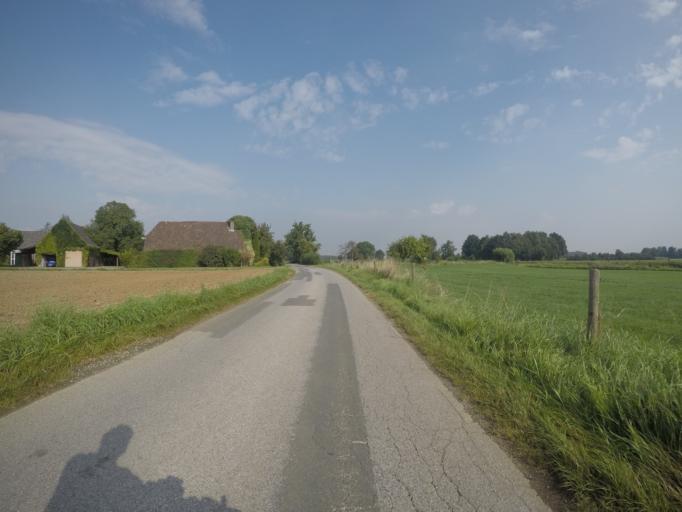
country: DE
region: North Rhine-Westphalia
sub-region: Regierungsbezirk Dusseldorf
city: Mehrhoog
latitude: 51.7988
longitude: 6.5404
